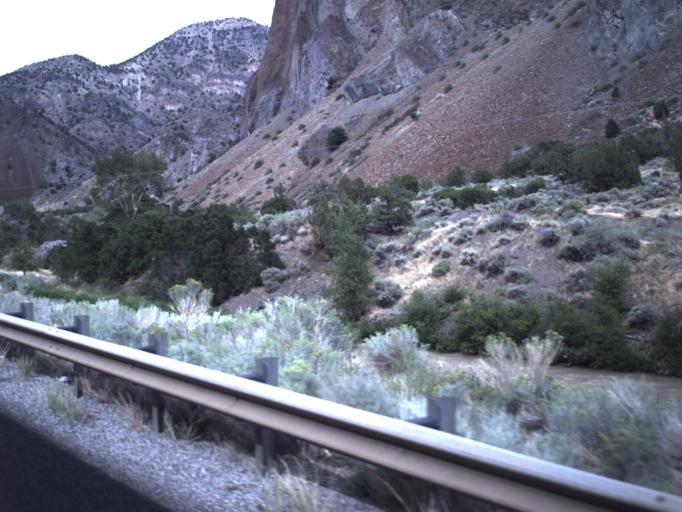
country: US
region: Utah
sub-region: Sevier County
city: Monroe
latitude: 38.5432
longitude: -112.2692
